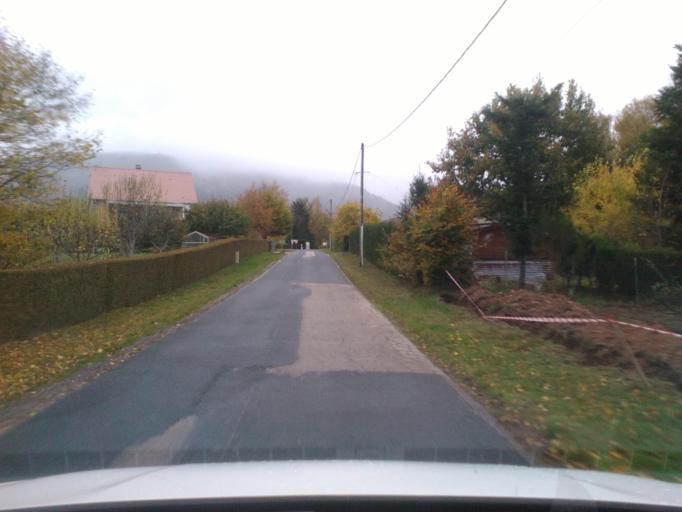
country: FR
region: Lorraine
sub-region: Departement des Vosges
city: Sainte-Marguerite
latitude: 48.2829
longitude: 6.9974
